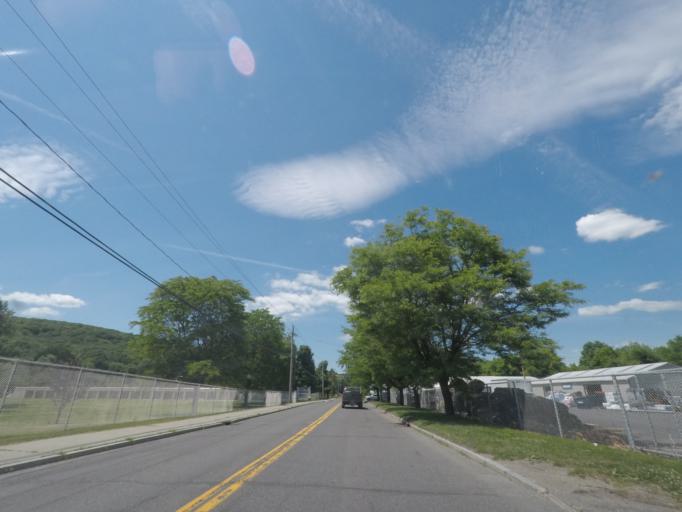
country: US
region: New York
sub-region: Dutchess County
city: Pine Plains
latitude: 41.9561
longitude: -73.5153
